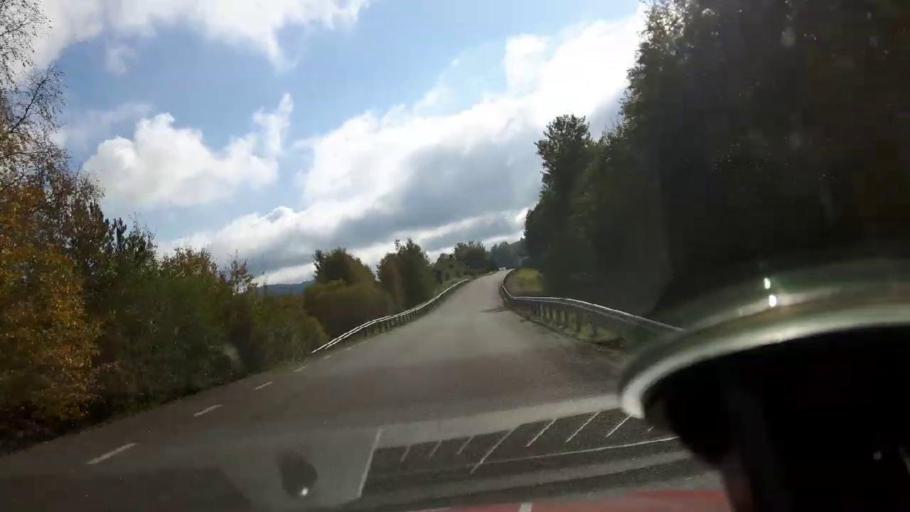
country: SE
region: Gaevleborg
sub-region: Ljusdals Kommun
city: Farila
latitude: 61.7784
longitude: 15.9470
